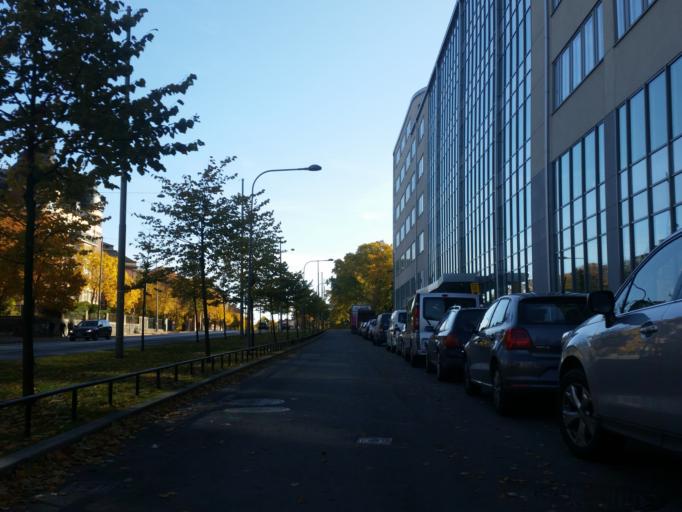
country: SE
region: Stockholm
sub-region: Stockholms Kommun
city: Arsta
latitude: 59.3103
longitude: 18.0586
